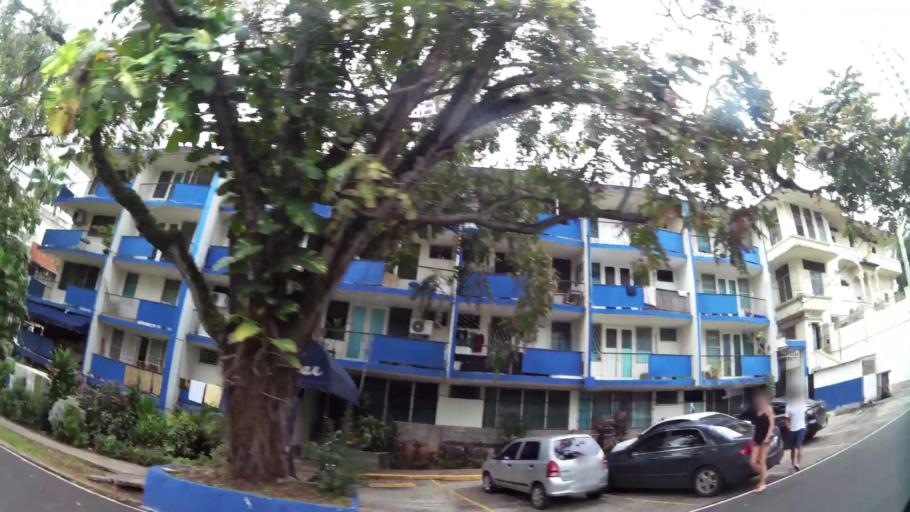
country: PA
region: Panama
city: Panama
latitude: 8.9768
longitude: -79.5286
